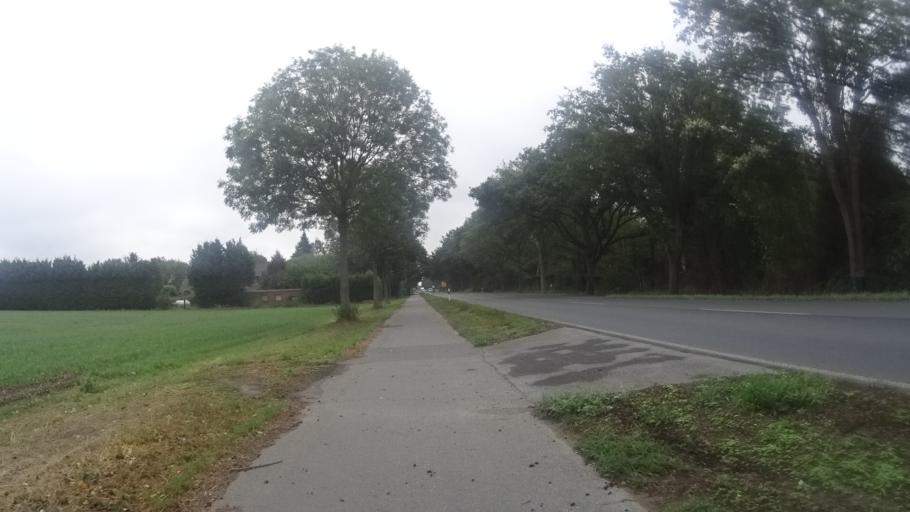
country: DE
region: North Rhine-Westphalia
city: Geldern
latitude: 51.5252
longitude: 6.3645
